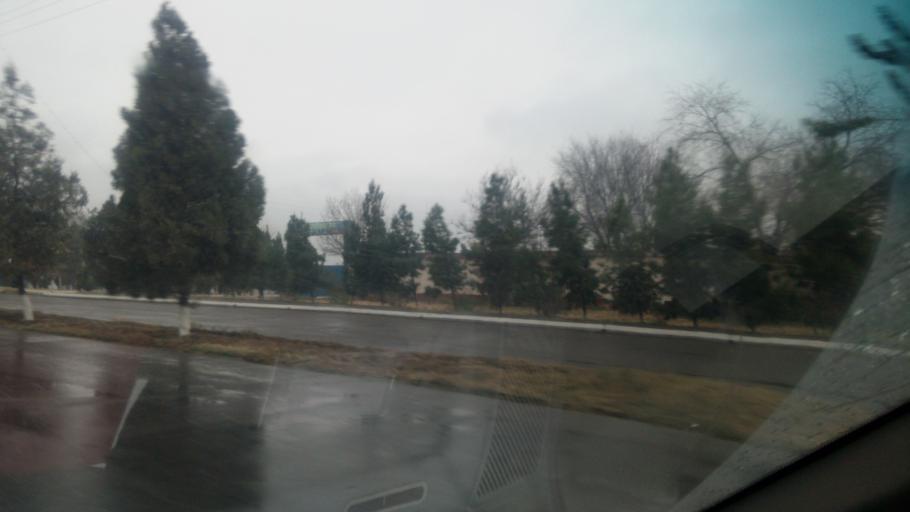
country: UZ
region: Toshkent
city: Urtaowul
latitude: 41.2334
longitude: 69.1583
